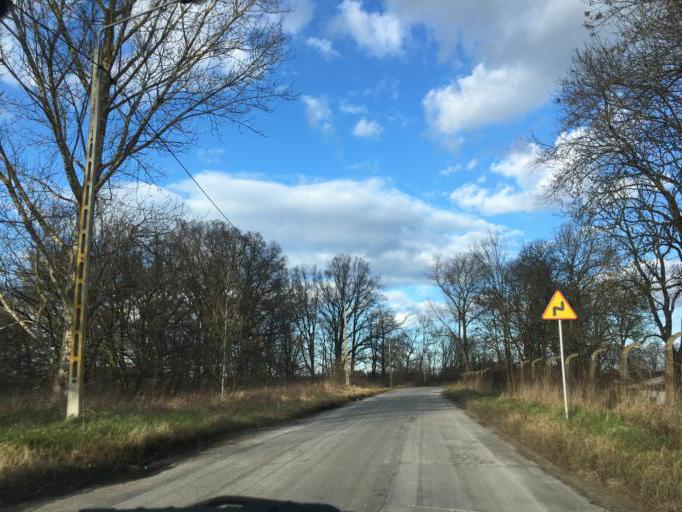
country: PL
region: Pomeranian Voivodeship
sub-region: Powiat nowodworski
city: Ostaszewo
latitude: 54.3112
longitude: 18.9263
